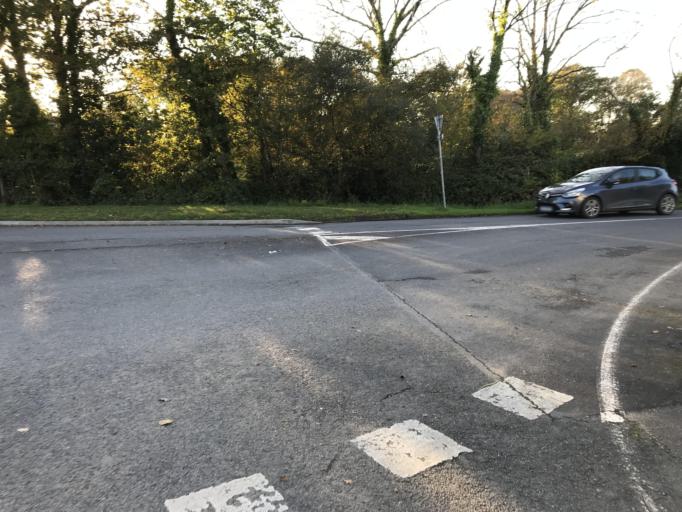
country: FR
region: Brittany
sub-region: Departement du Finistere
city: Le Faou
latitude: 48.2940
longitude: -4.1815
